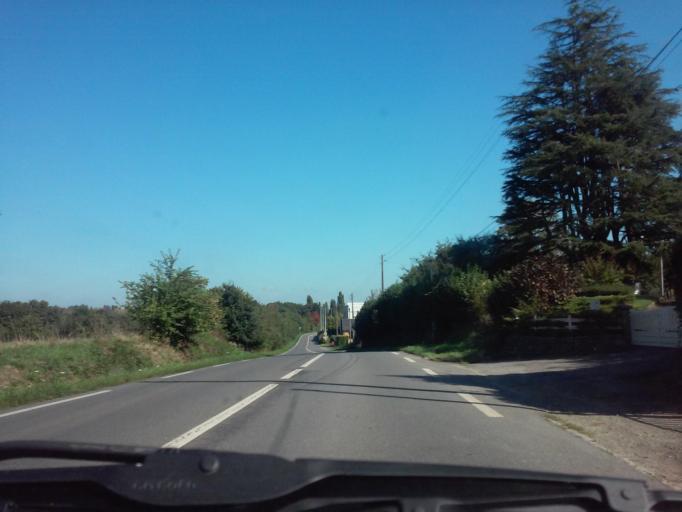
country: FR
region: Brittany
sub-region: Departement d'Ille-et-Vilaine
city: Betton
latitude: 48.1657
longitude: -1.6455
